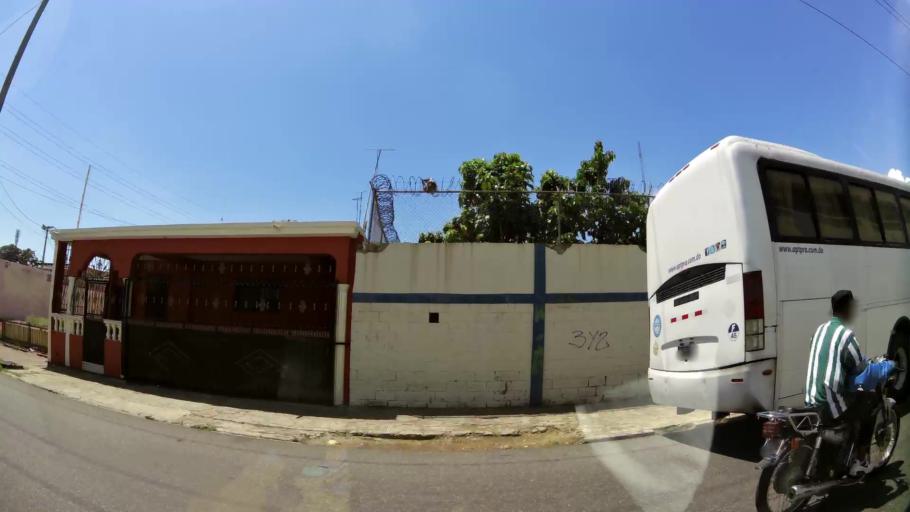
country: DO
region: Nacional
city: San Carlos
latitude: 18.4896
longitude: -69.8899
